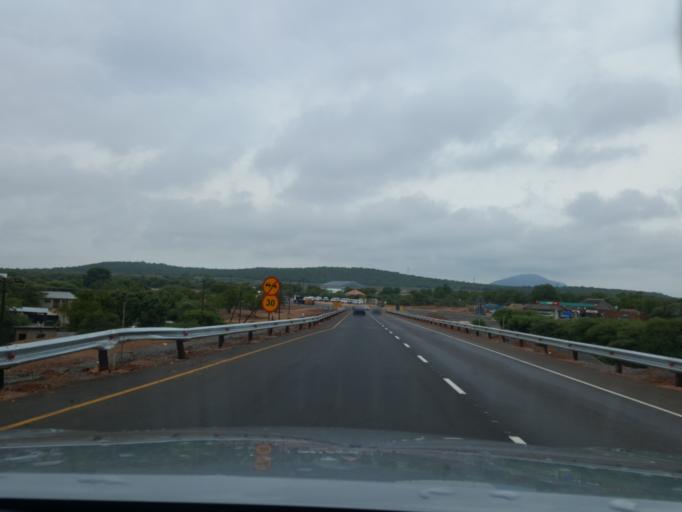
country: BW
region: South East
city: Ramotswa
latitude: -24.8284
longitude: 25.8069
